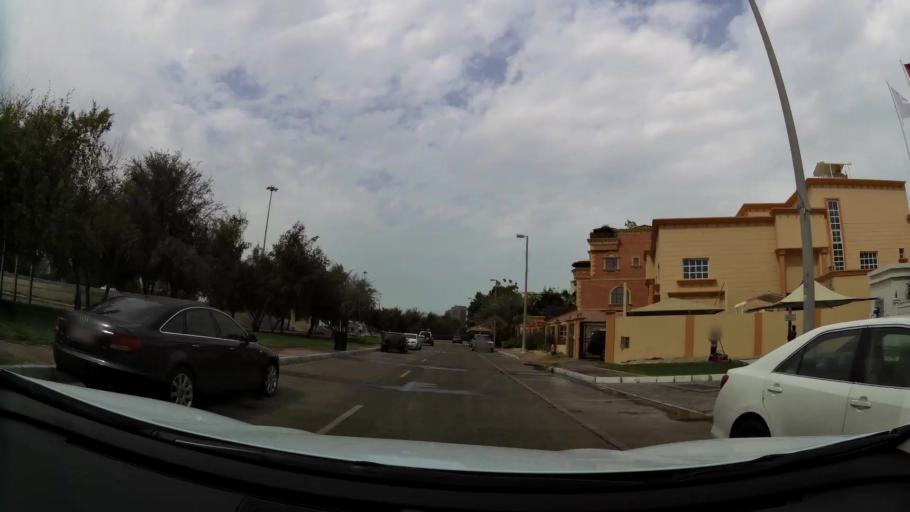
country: AE
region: Abu Dhabi
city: Abu Dhabi
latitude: 24.4264
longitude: 54.4480
